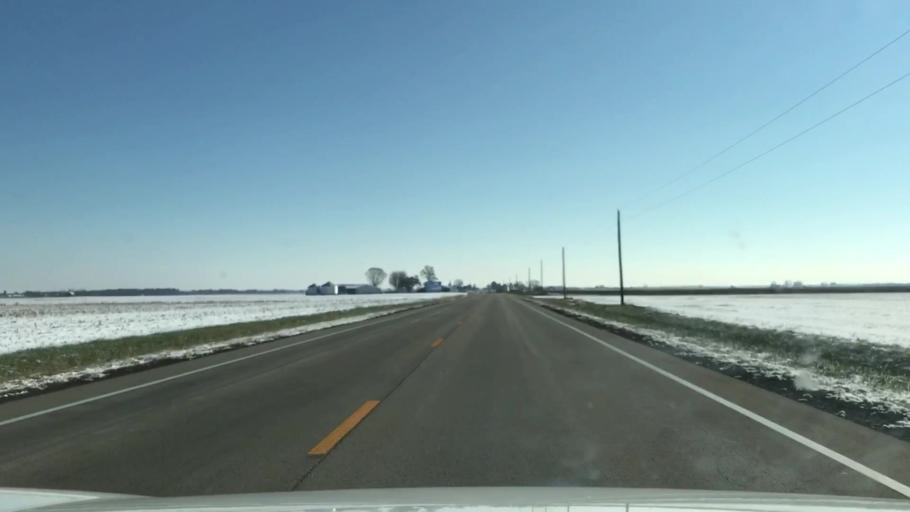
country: US
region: Illinois
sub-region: Washington County
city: Okawville
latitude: 38.4428
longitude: -89.5163
